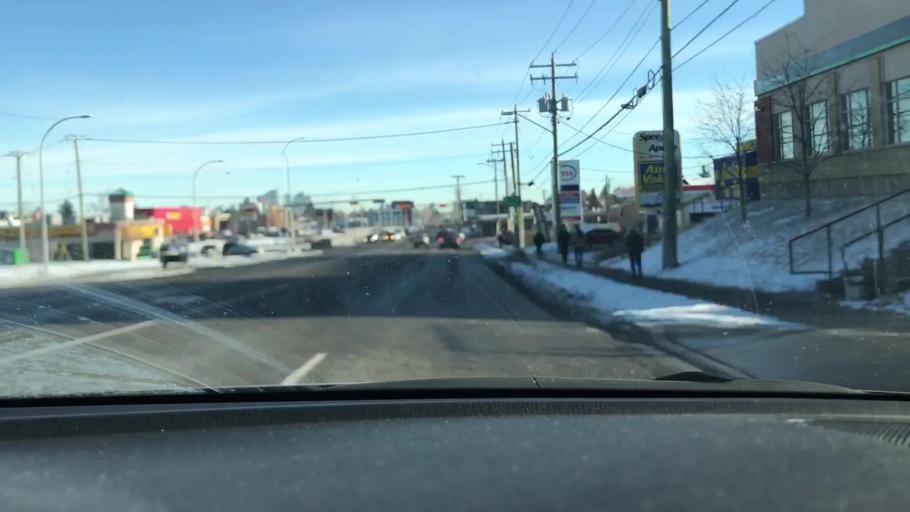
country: CA
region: Alberta
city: Calgary
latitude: 51.0378
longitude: -114.1431
